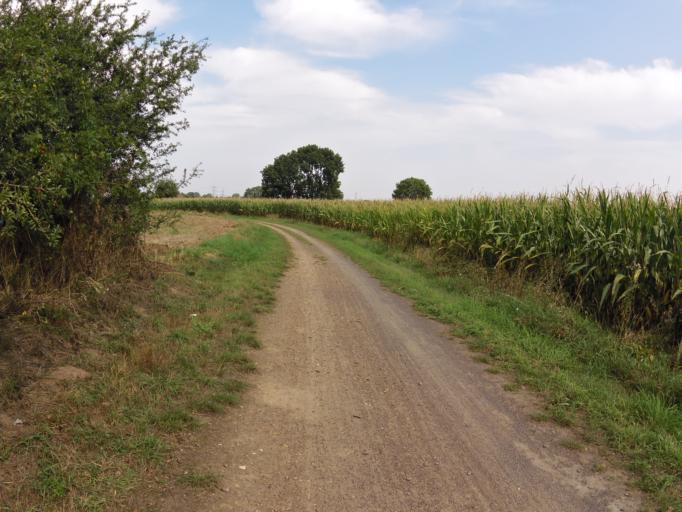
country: DE
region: Lower Saxony
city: Stolzenau
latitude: 52.5268
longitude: 9.0803
